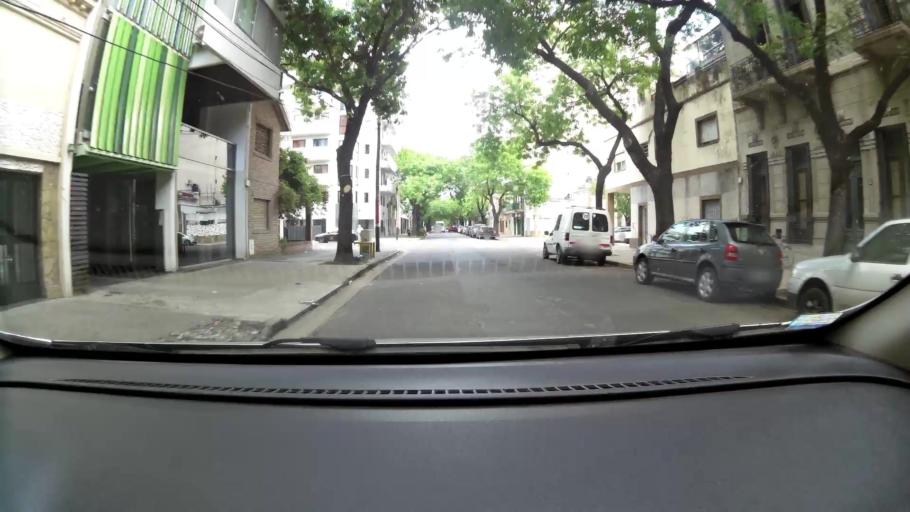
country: AR
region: Santa Fe
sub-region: Departamento de Rosario
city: Rosario
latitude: -32.9605
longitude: -60.6345
